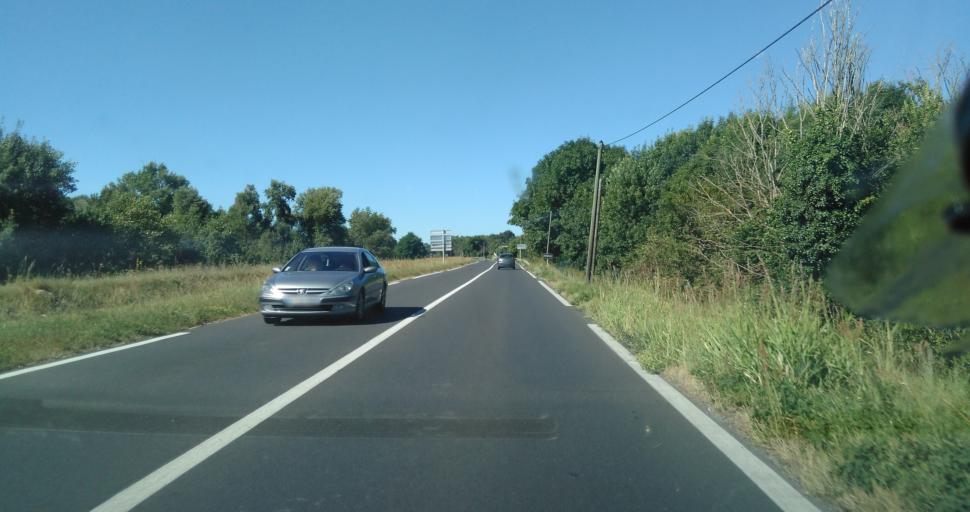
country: FR
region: Centre
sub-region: Departement d'Indre-et-Loire
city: Nazelles-Negron
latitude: 47.4122
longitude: 0.9590
